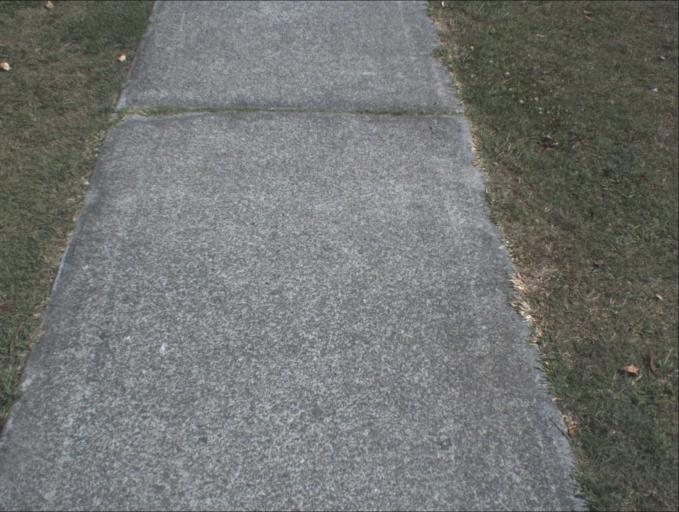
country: AU
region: Queensland
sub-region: Logan
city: Beenleigh
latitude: -27.6744
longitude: 153.2079
